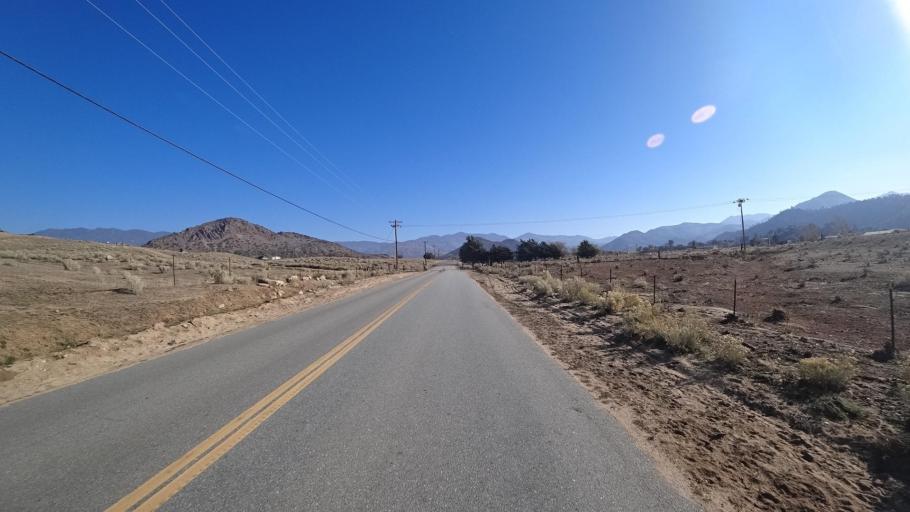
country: US
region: California
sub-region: Kern County
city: Tehachapi
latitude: 35.3177
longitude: -118.3963
